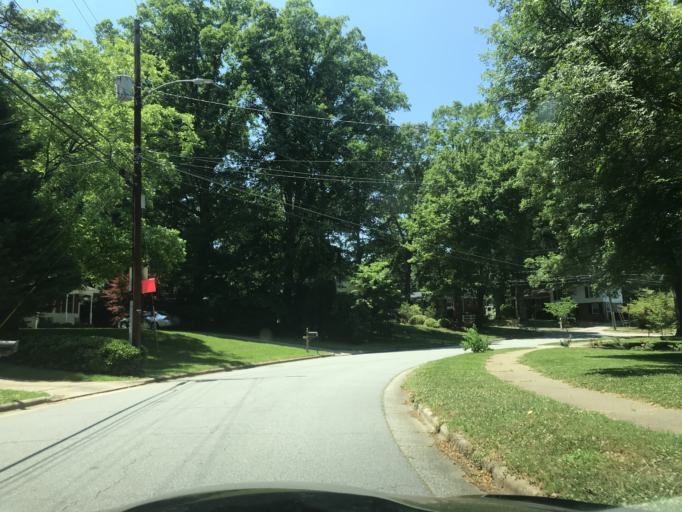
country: US
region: North Carolina
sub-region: Wake County
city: West Raleigh
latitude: 35.8431
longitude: -78.6346
